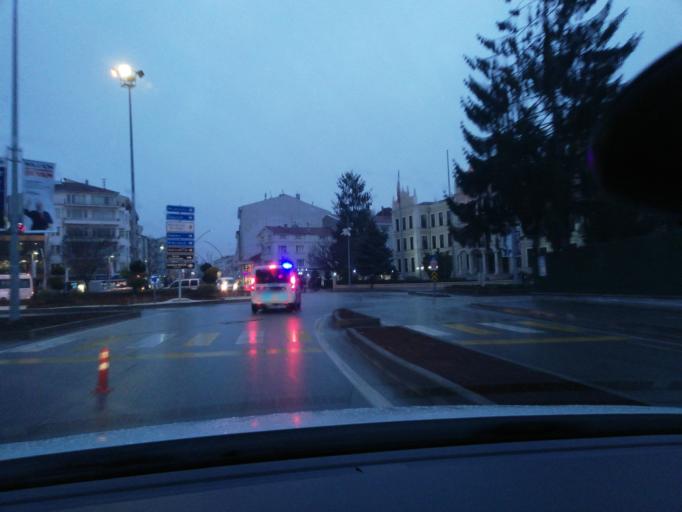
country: TR
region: Bolu
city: Bolu
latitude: 40.7305
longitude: 31.5995
